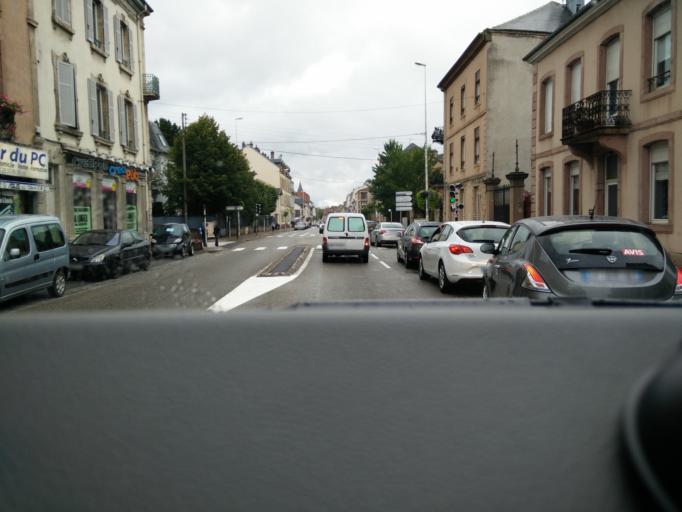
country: FR
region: Lorraine
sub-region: Departement des Vosges
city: Saint-Die-des-Vosges
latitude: 48.2804
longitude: 6.9550
